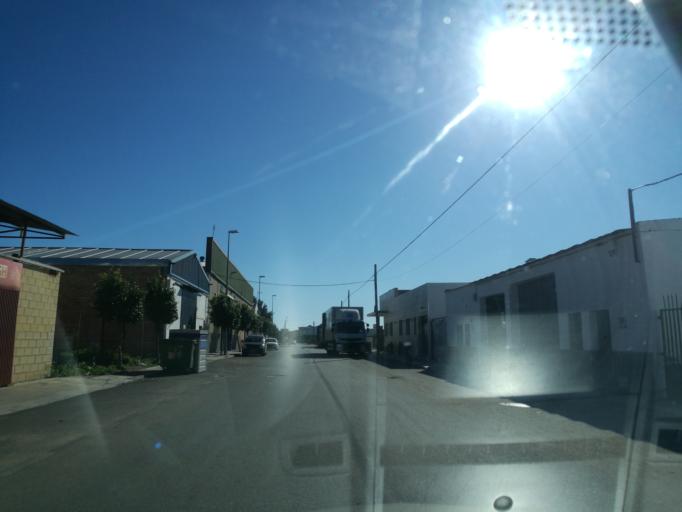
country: ES
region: Andalusia
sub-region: Provincia de Sevilla
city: La Campana
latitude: 37.5749
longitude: -5.4316
